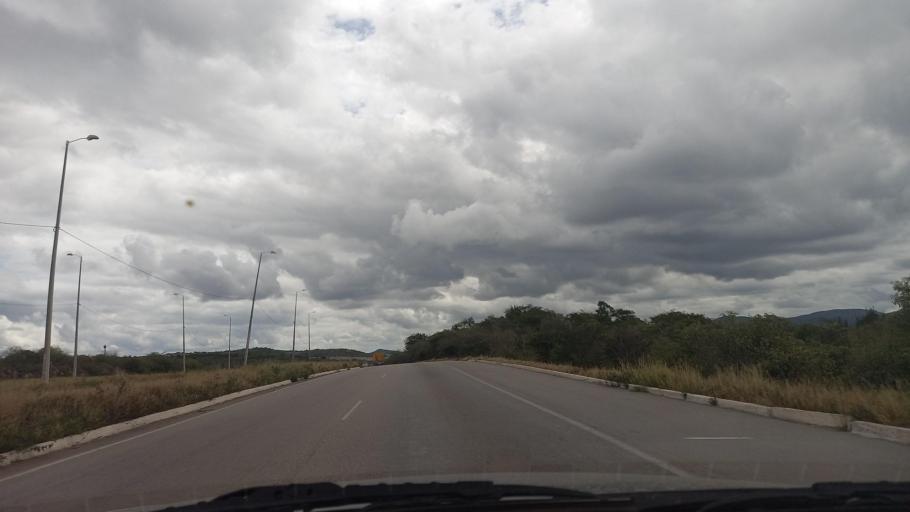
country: BR
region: Pernambuco
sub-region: Caruaru
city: Caruaru
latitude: -8.3209
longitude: -36.0851
